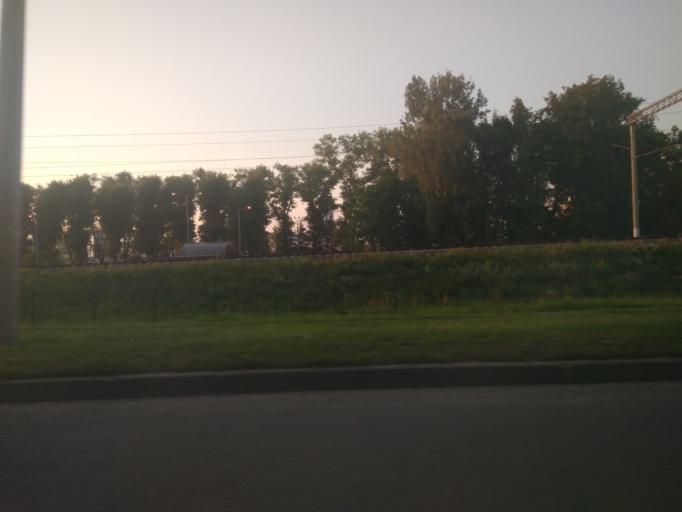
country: BY
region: Minsk
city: Zhdanovichy
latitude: 53.9306
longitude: 27.4669
